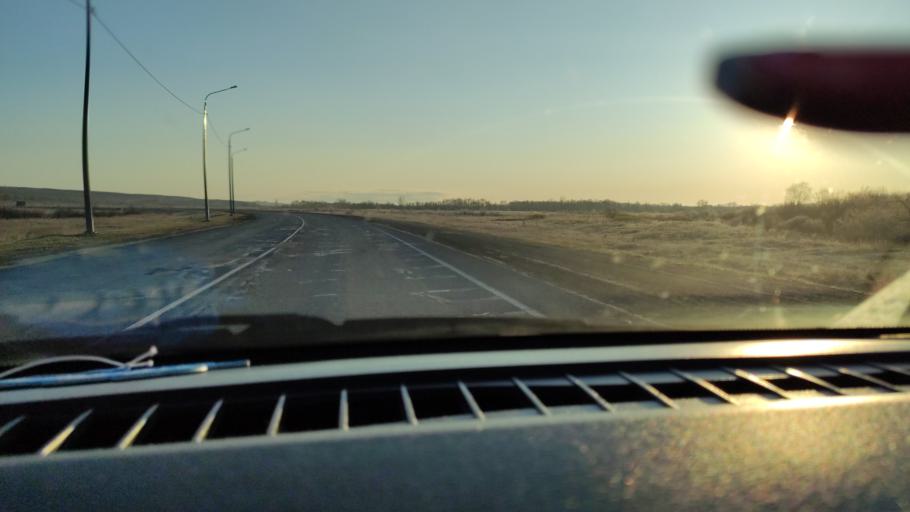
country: RU
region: Saratov
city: Sennoy
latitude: 52.0897
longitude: 46.8090
